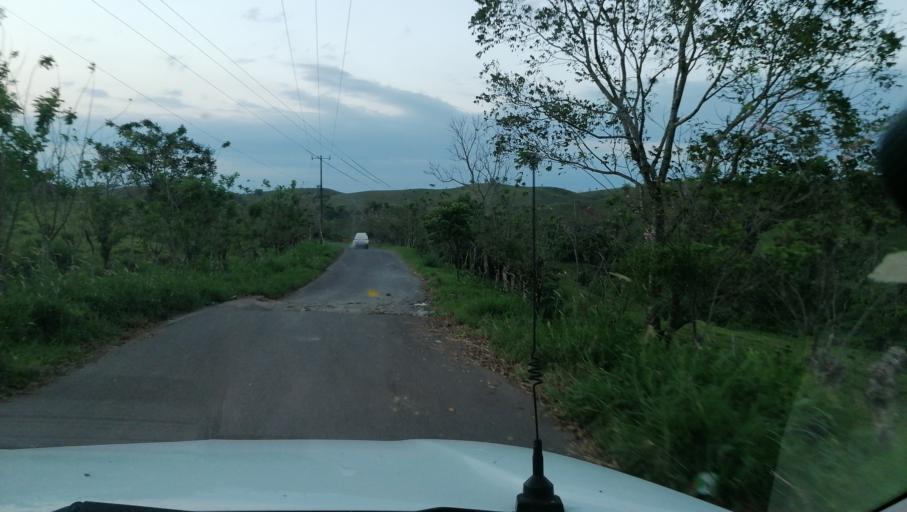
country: MX
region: Chiapas
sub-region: Ostuacan
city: Nuevo Juan del Grijalva
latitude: 17.4399
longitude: -93.3509
